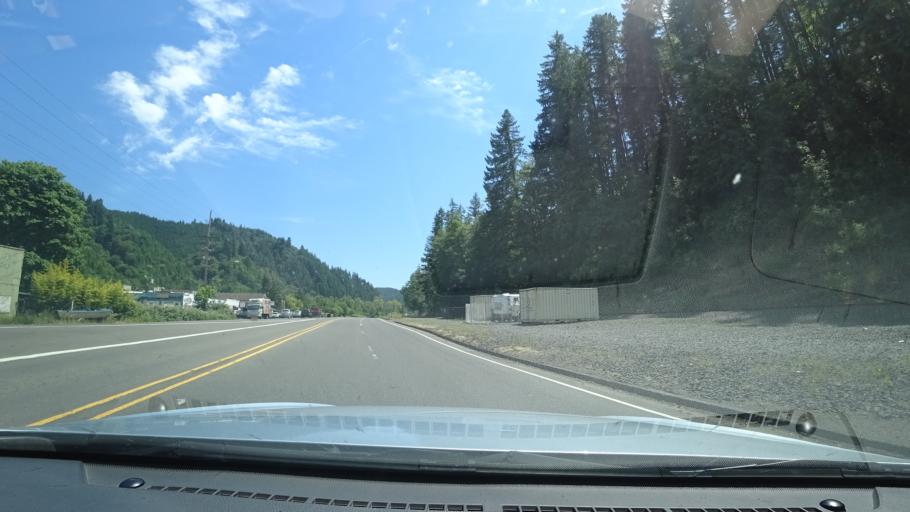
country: US
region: Oregon
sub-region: Lane County
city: Florence
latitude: 44.0311
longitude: -123.8595
